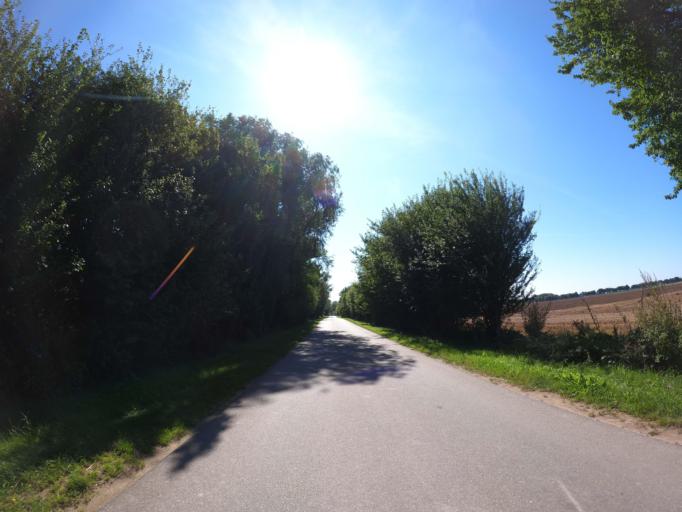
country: DE
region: Mecklenburg-Vorpommern
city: Prohn
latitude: 54.3834
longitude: 13.0258
